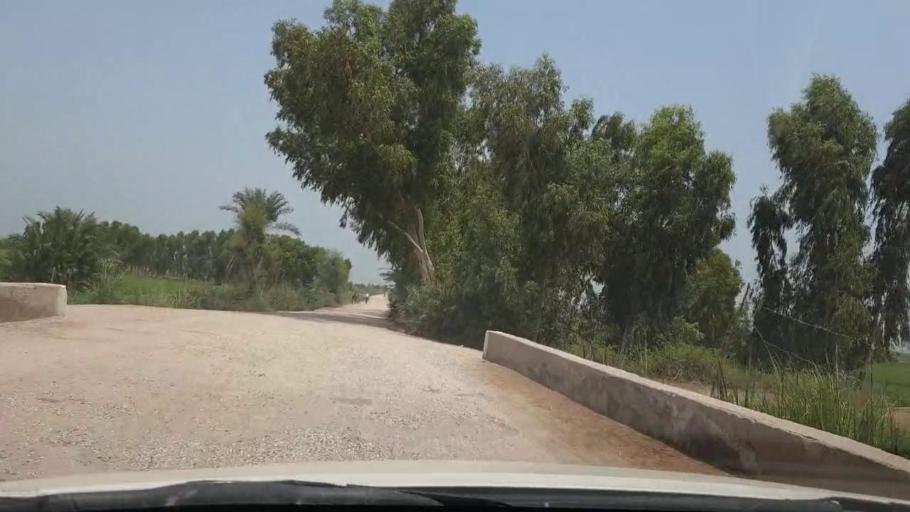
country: PK
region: Sindh
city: Rustam jo Goth
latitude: 28.0239
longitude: 68.8127
